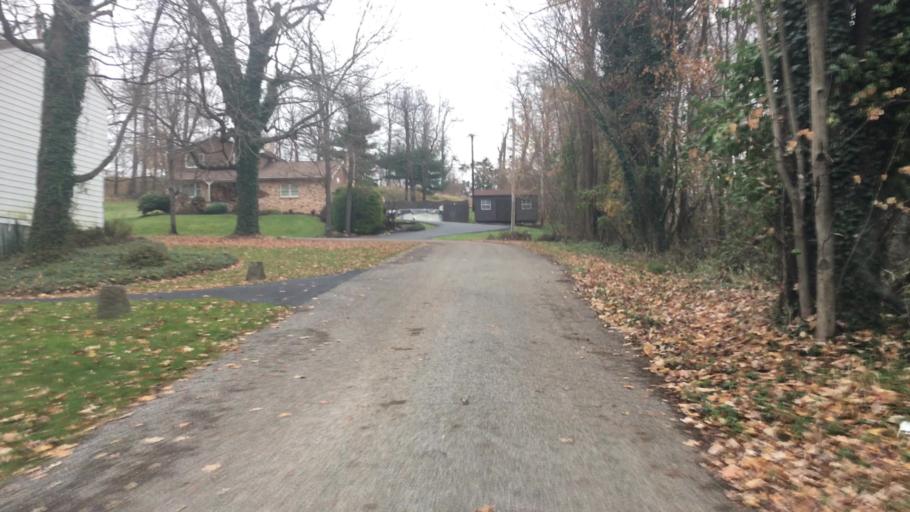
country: US
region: Pennsylvania
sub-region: Lawrence County
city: Bessemer
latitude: 40.9620
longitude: -80.4313
